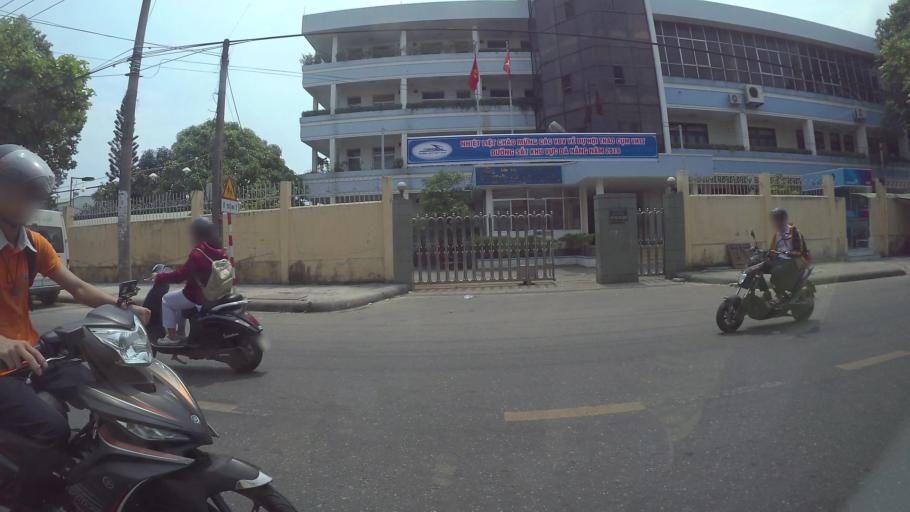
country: VN
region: Da Nang
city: Da Nang
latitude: 16.0722
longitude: 108.2071
